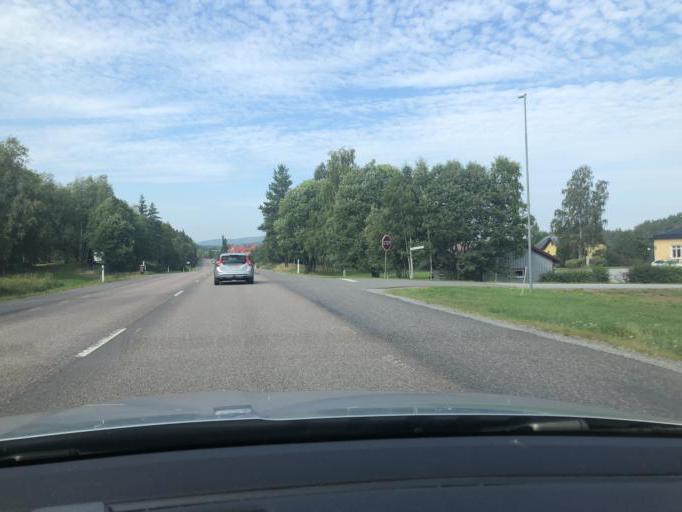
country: SE
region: Vaesternorrland
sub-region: Kramfors Kommun
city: Kramfors
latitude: 62.9059
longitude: 17.8244
